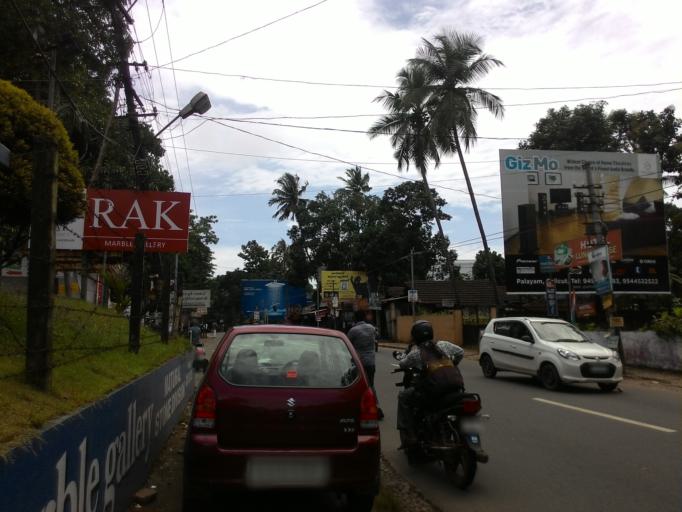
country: IN
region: Kerala
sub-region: Kozhikode
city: Kozhikode
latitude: 11.2851
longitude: 75.7919
